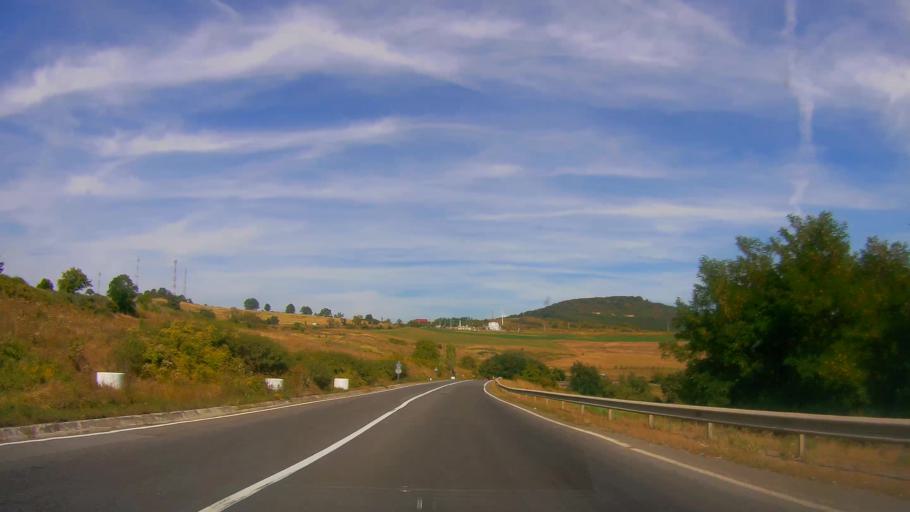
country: RO
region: Mures
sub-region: Comuna Nades
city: Nades
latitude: 46.2699
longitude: 24.7358
